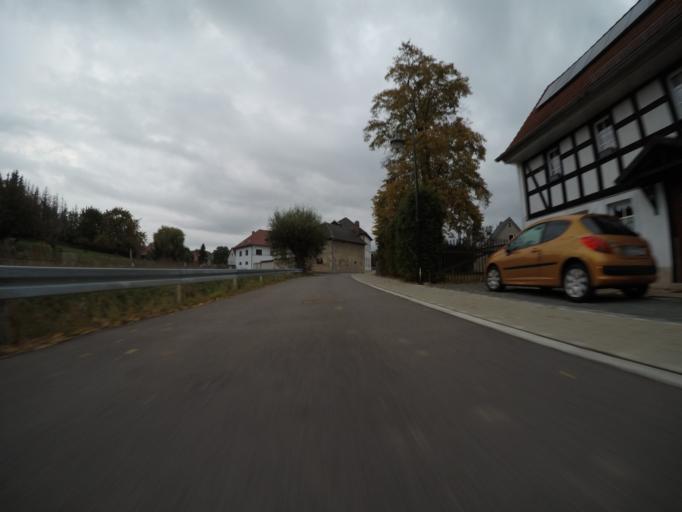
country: DE
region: Thuringia
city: Schmolln
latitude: 50.9074
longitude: 12.3739
